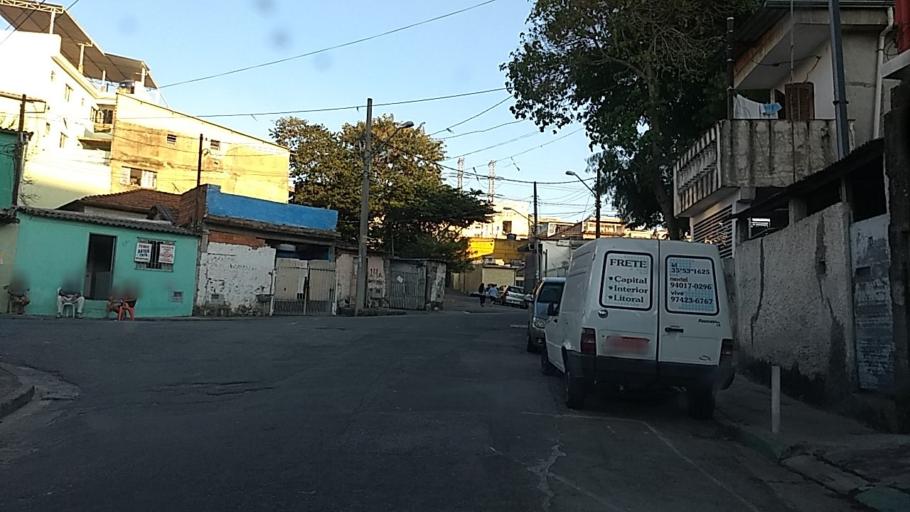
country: BR
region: Sao Paulo
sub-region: Guarulhos
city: Guarulhos
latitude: -23.4972
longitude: -46.5908
